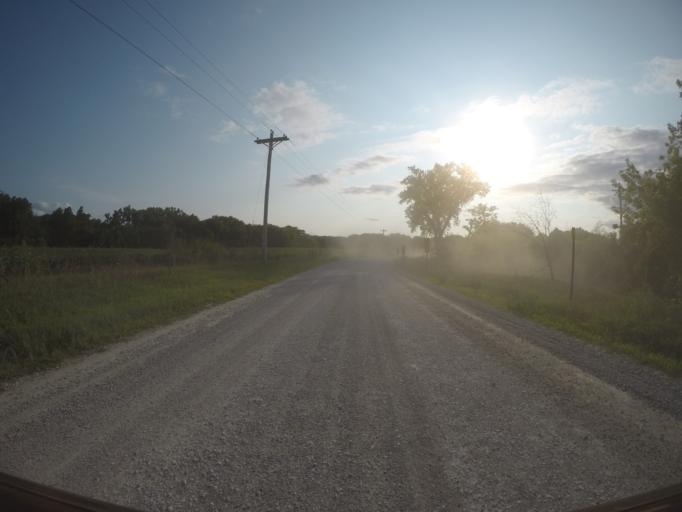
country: US
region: Kansas
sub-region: Wabaunsee County
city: Alma
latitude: 38.9925
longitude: -96.2751
